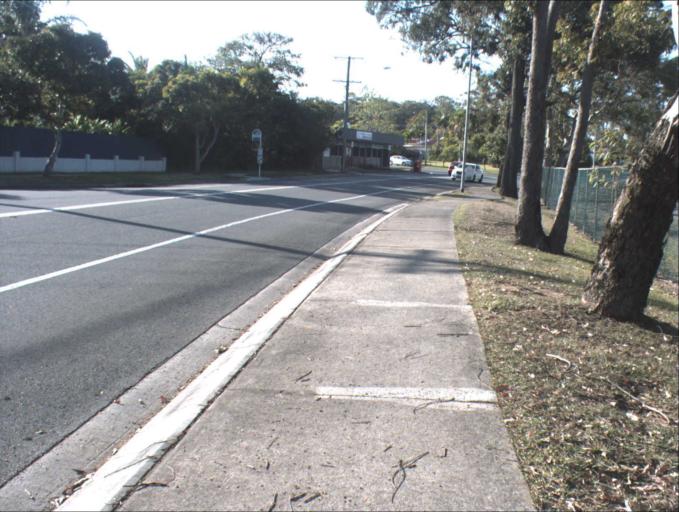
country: AU
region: Queensland
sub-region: Logan
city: Woodridge
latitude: -27.6341
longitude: 153.0981
